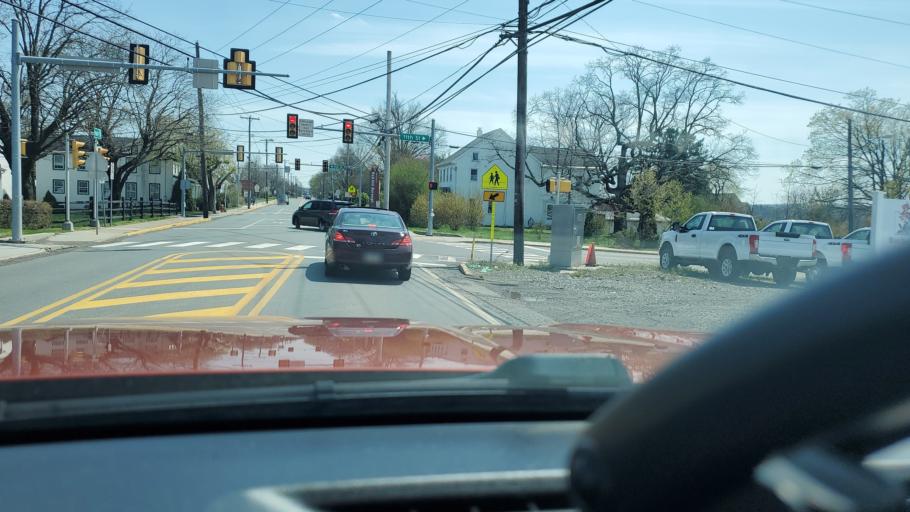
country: US
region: Pennsylvania
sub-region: Montgomery County
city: Pennsburg
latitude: 40.3850
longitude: -75.4883
